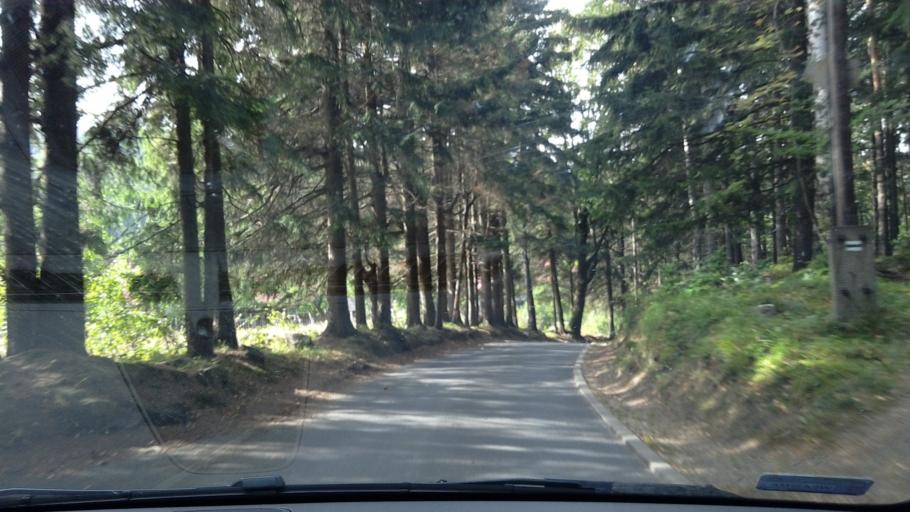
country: PL
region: Lower Silesian Voivodeship
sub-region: Powiat jeleniogorski
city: Karpacz
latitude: 50.7697
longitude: 15.7494
